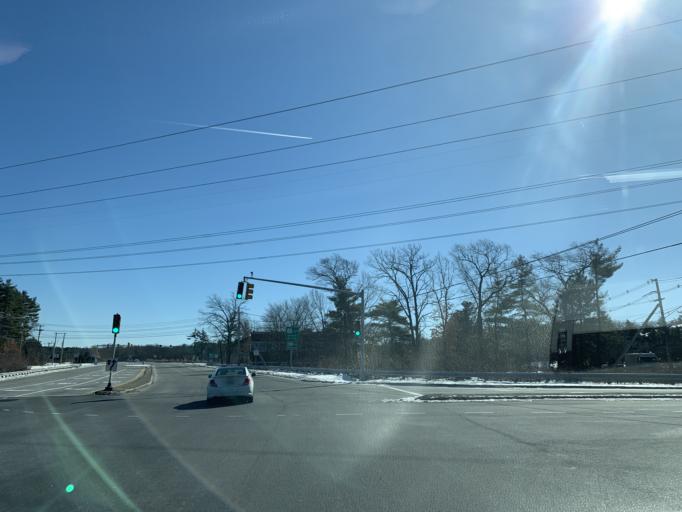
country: US
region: Massachusetts
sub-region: Middlesex County
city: Lowell
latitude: 42.5903
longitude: -71.3167
